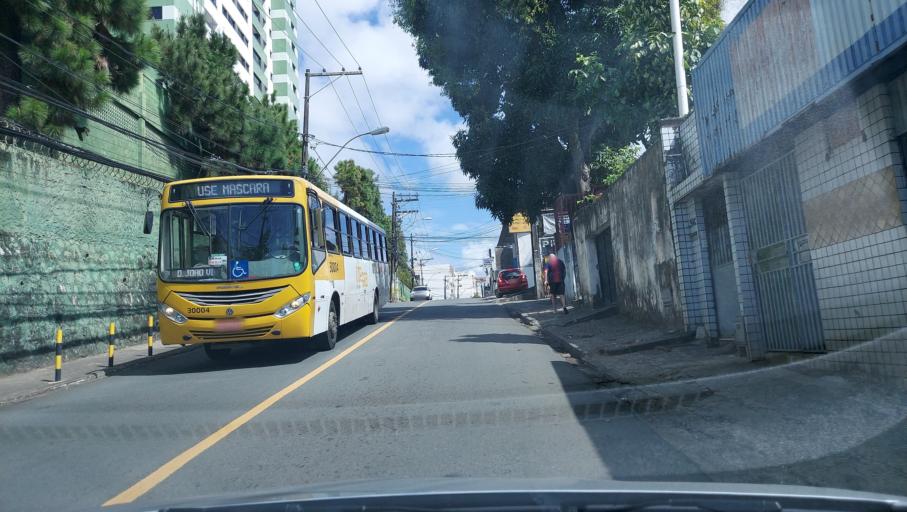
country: BR
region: Bahia
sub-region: Salvador
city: Salvador
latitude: -12.9918
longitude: -38.4775
